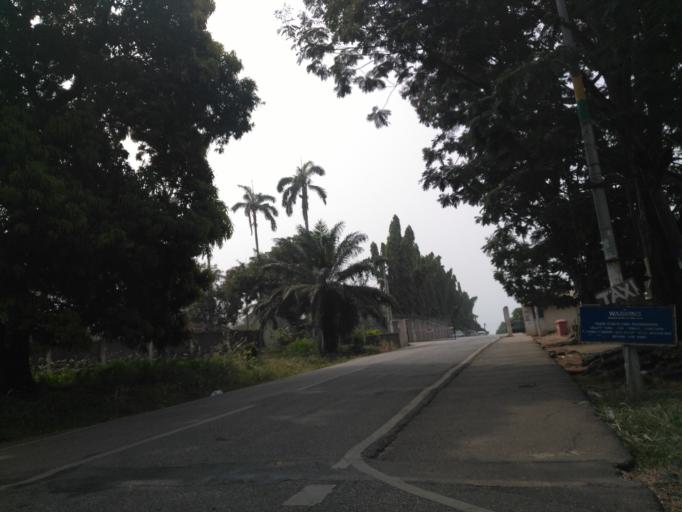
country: GH
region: Ashanti
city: Kumasi
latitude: 6.6779
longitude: -1.6295
